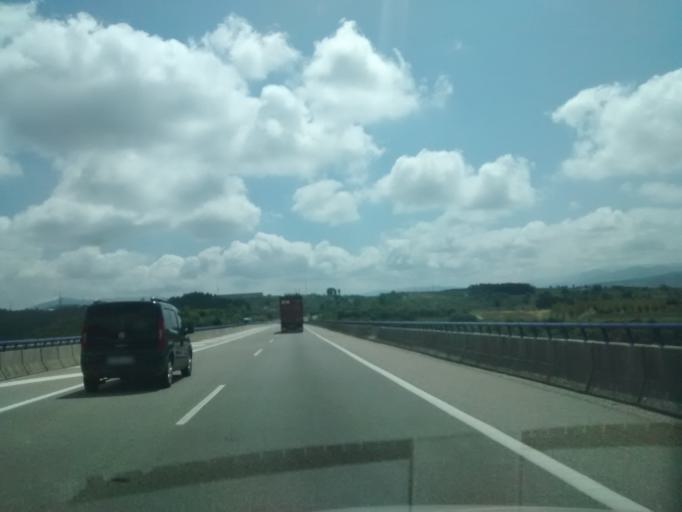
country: ES
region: Castille and Leon
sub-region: Provincia de Leon
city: Ponferrada
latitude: 42.5668
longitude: -6.5791
